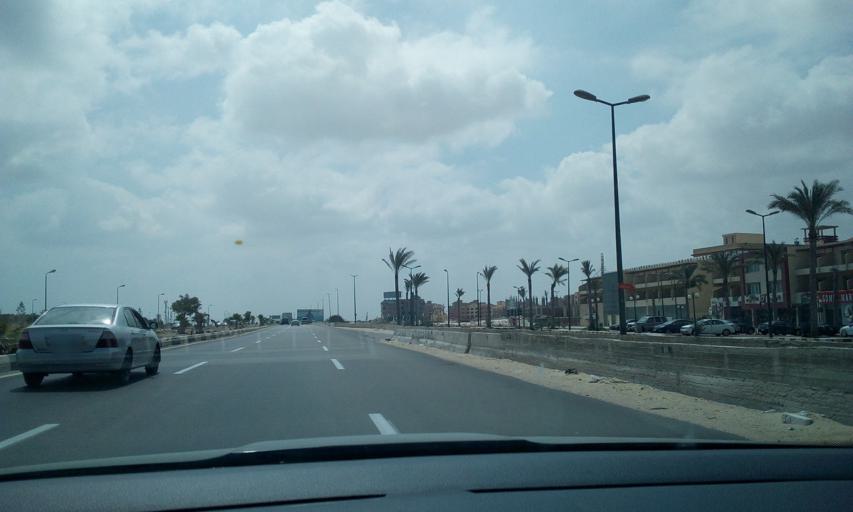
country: EG
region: Muhafazat Matruh
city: Al `Alamayn
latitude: 30.8294
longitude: 28.9715
